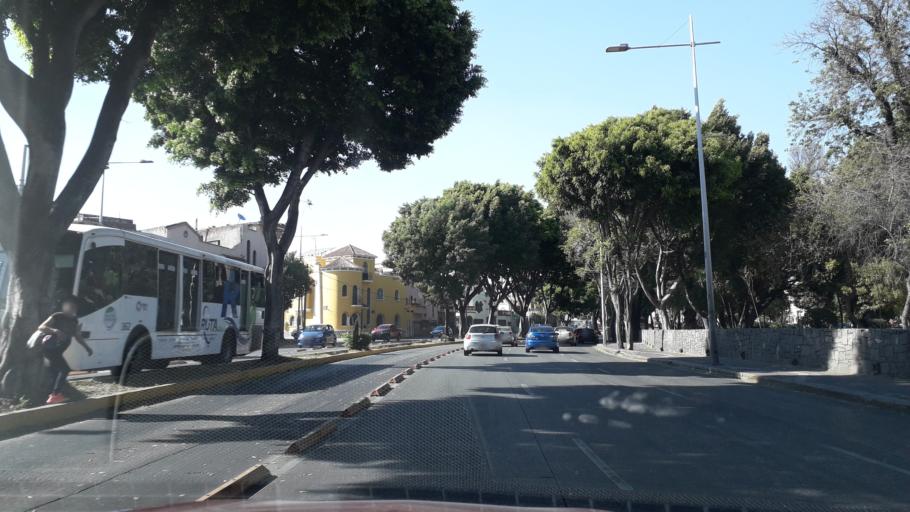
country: MX
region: Puebla
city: Puebla
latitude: 19.0467
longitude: -98.1896
